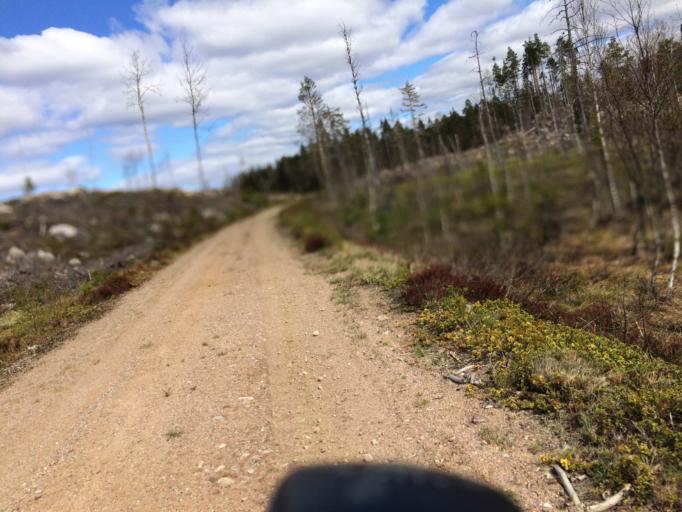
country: SE
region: OErebro
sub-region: Hallefors Kommun
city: Haellefors
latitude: 60.0525
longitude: 14.5236
